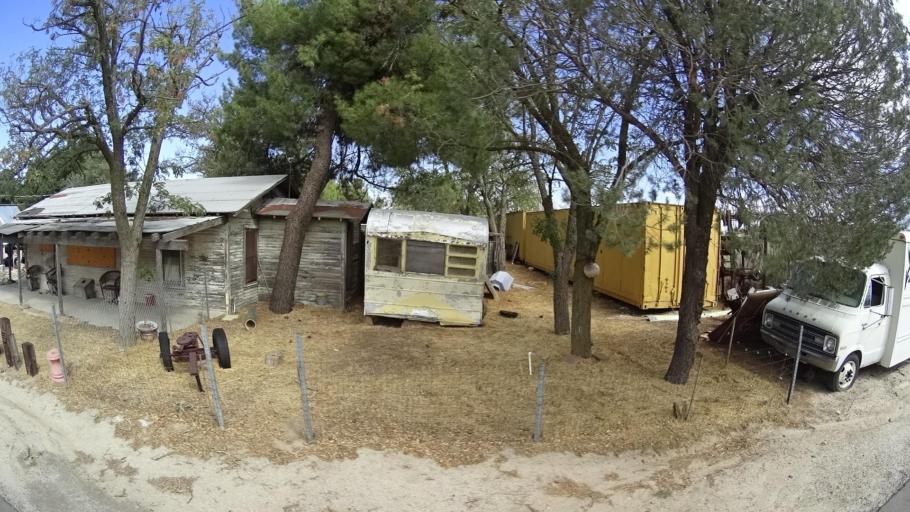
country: MX
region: Baja California
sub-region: Tecate
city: Cereso del Hongo
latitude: 32.6685
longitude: -116.2901
